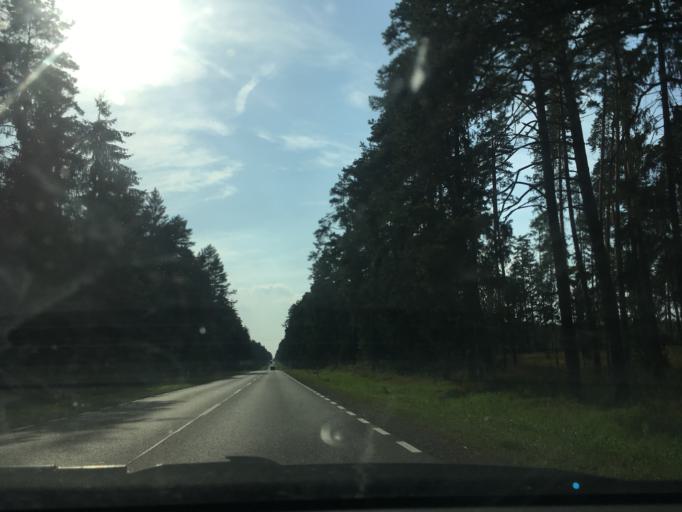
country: PL
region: Podlasie
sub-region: Powiat bialostocki
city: Suprasl
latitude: 53.1256
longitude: 23.3482
